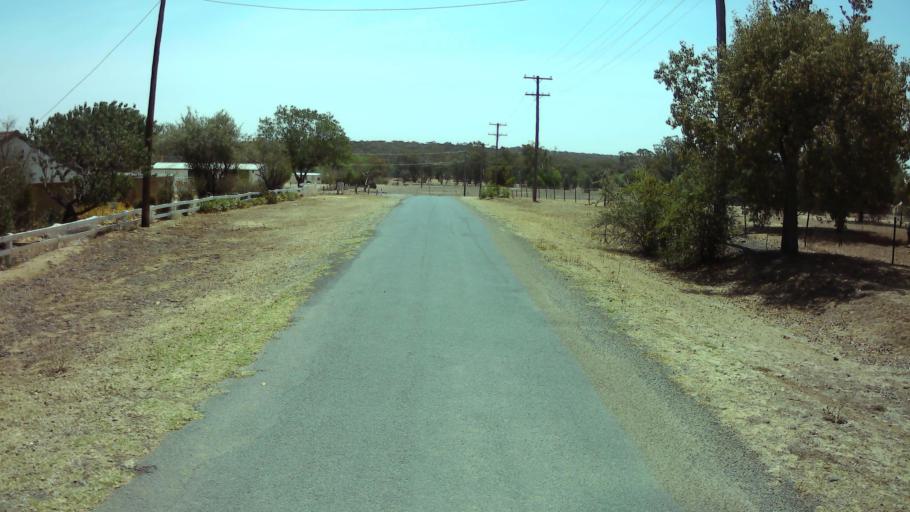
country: AU
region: New South Wales
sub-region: Weddin
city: Grenfell
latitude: -33.8936
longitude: 148.1723
